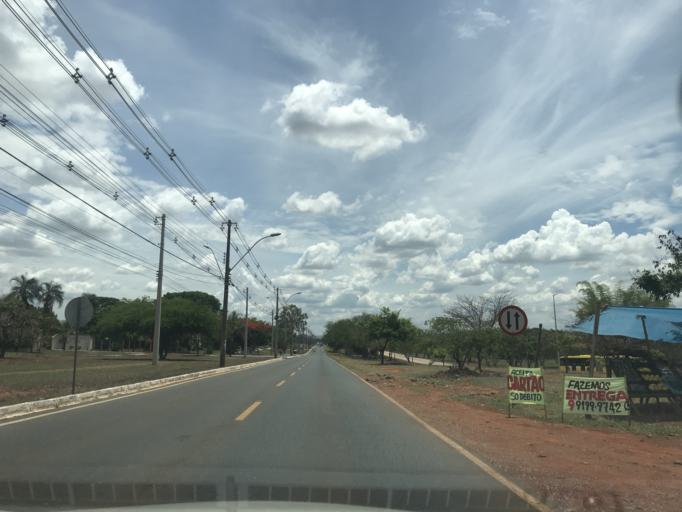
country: BR
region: Federal District
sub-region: Brasilia
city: Brasilia
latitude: -15.8680
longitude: -47.9426
